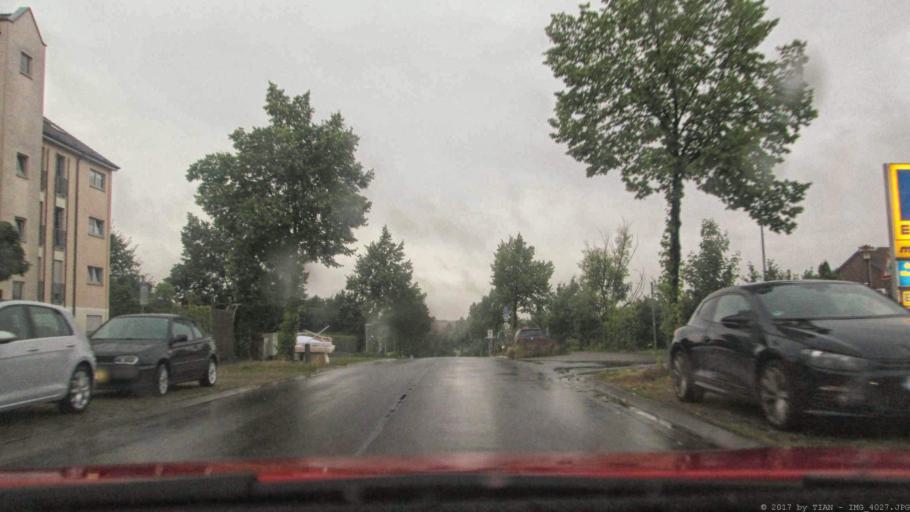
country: DE
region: Lower Saxony
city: Wolfsburg
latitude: 52.4140
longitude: 10.8404
